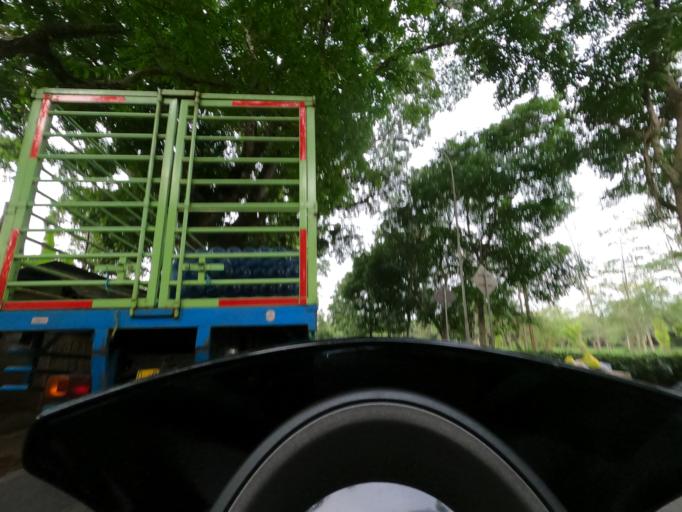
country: ID
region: West Java
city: Lembang
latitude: -6.6749
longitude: 107.6958
